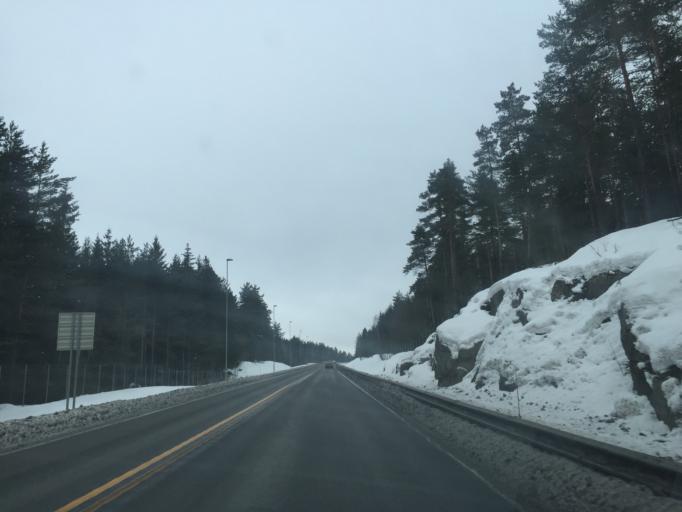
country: NO
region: Hedmark
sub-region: Loten
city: Loten
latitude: 60.7448
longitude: 11.3002
